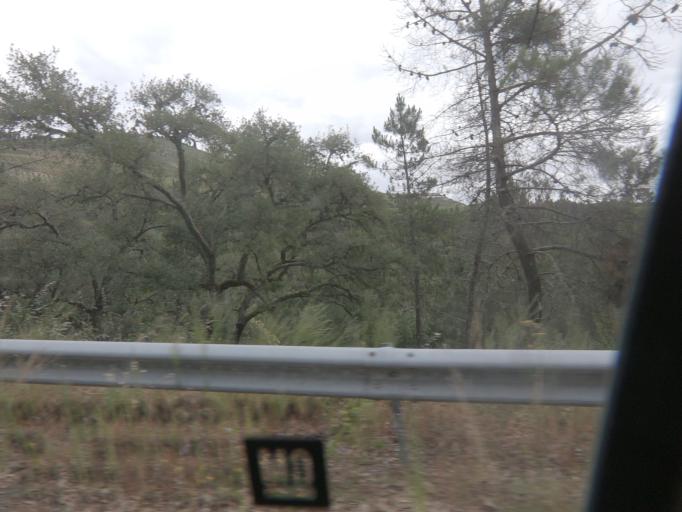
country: PT
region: Vila Real
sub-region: Sabrosa
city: Vilela
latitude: 41.2024
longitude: -7.5643
